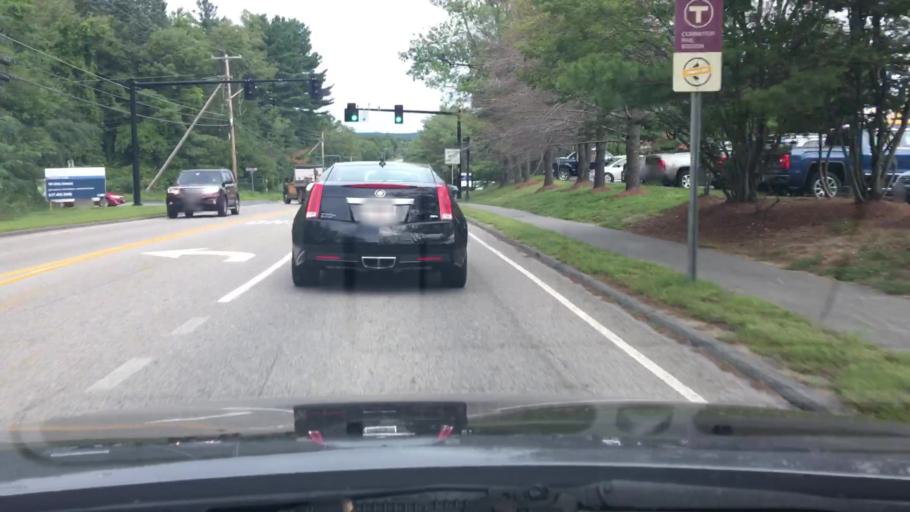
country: US
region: Massachusetts
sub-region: Worcester County
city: Westborough
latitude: 42.2719
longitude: -71.6427
